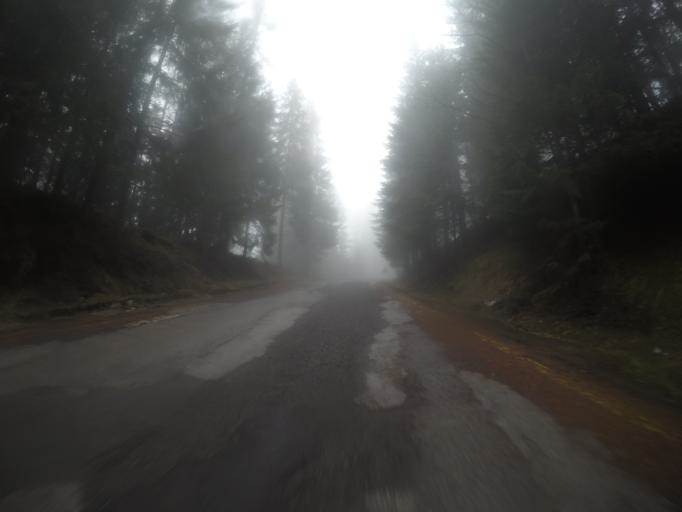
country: SK
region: Presovsky
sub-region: Okres Poprad
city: Strba
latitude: 49.1273
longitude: 20.0734
